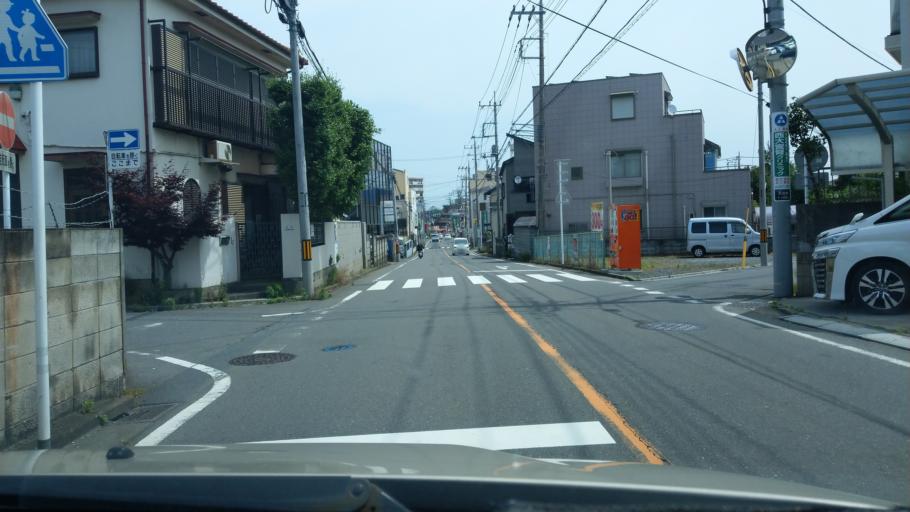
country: JP
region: Saitama
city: Saitama
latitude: 35.9096
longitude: 139.6408
